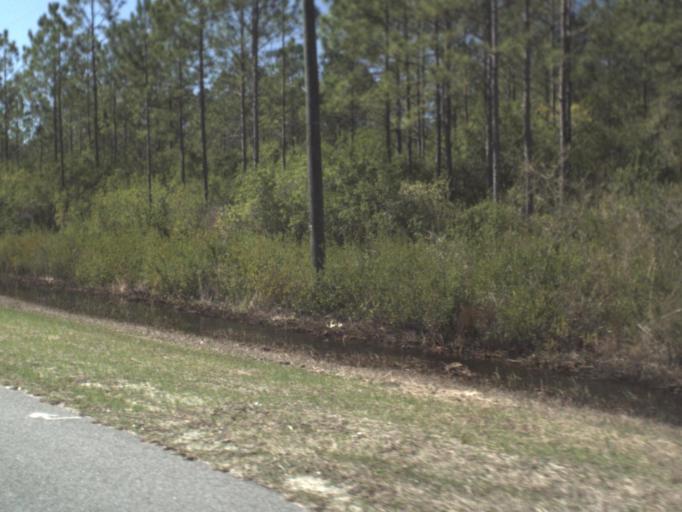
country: US
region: Florida
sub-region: Bay County
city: Laguna Beach
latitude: 30.3049
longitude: -85.8241
